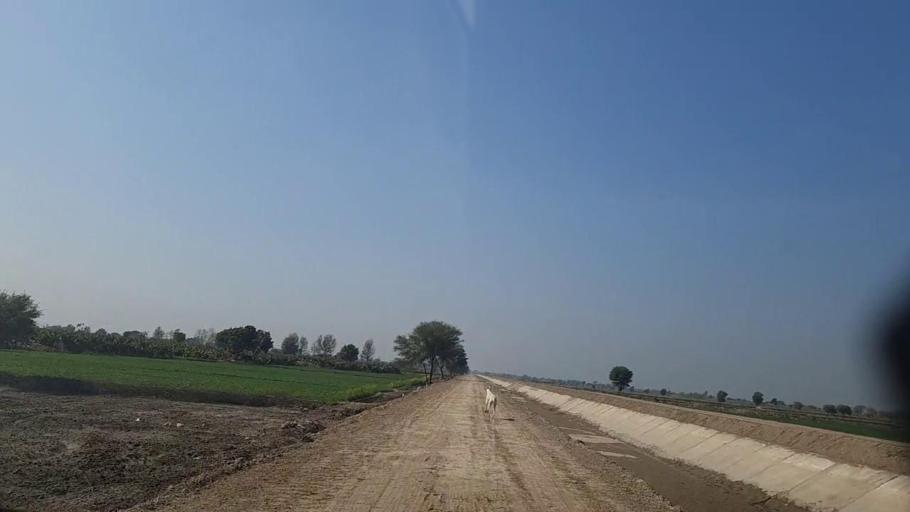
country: PK
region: Sindh
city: Sakrand
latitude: 26.1472
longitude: 68.3599
